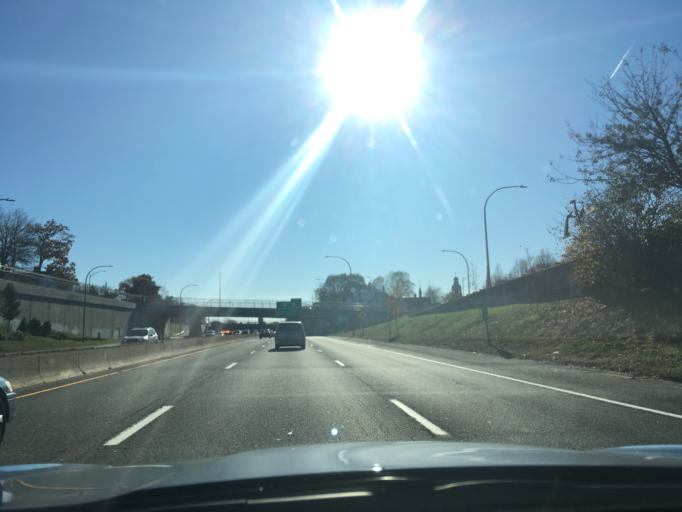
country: US
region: Rhode Island
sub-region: Providence County
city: Pawtucket
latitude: 41.8797
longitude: -71.3782
